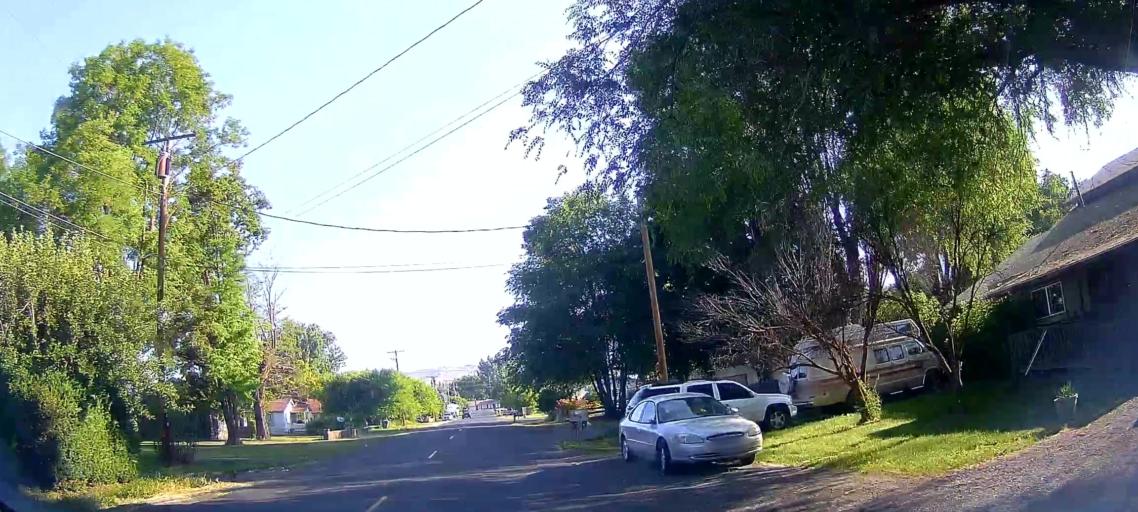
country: US
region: Oregon
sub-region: Klamath County
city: Altamont
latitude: 42.2113
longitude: -121.7487
